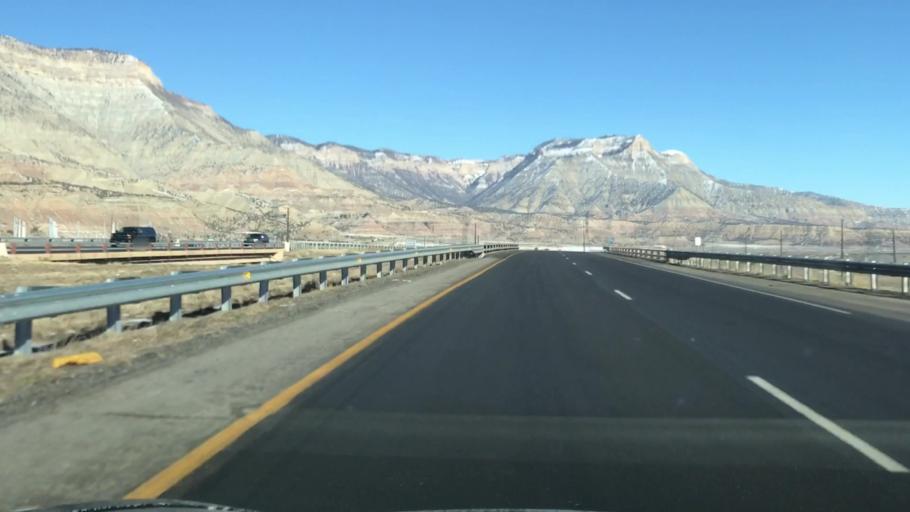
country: US
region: Colorado
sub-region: Garfield County
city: Parachute
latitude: 39.4600
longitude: -108.0448
